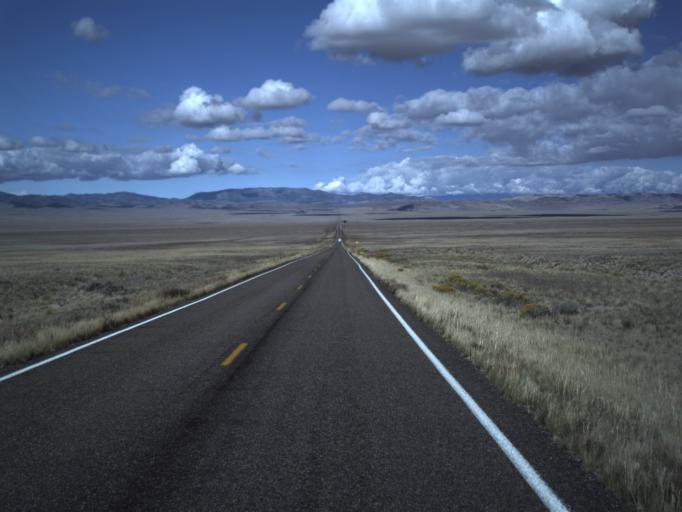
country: US
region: Utah
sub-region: Beaver County
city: Milford
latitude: 38.5149
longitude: -113.6348
